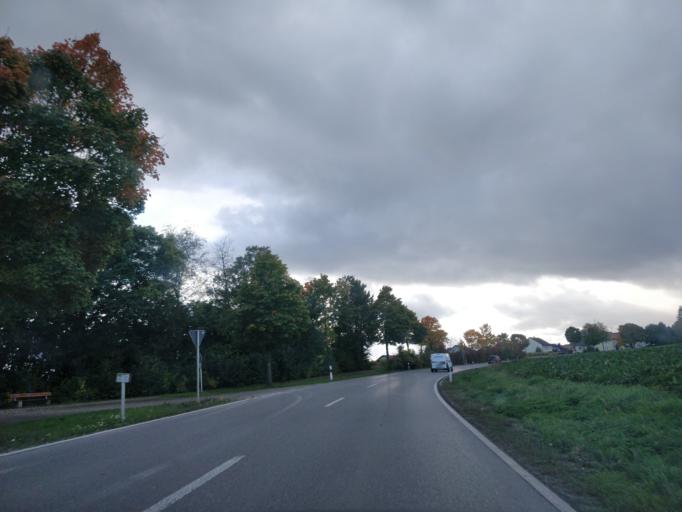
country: DE
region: Bavaria
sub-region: Swabia
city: Ried
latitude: 48.2841
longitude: 11.0297
